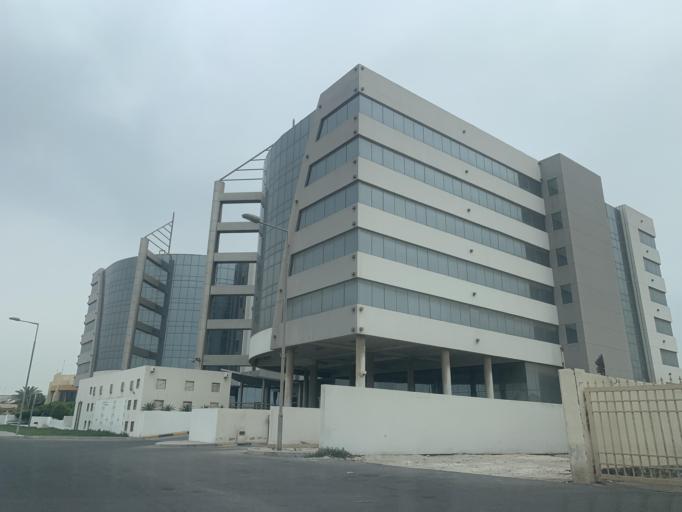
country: BH
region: Muharraq
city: Al Hadd
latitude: 26.2147
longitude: 50.6683
